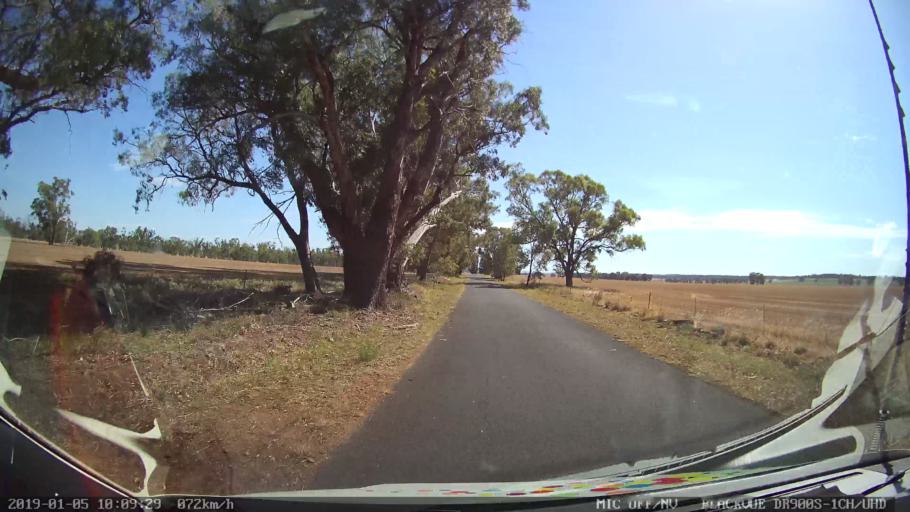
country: AU
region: New South Wales
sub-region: Gilgandra
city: Gilgandra
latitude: -31.6310
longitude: 148.8871
